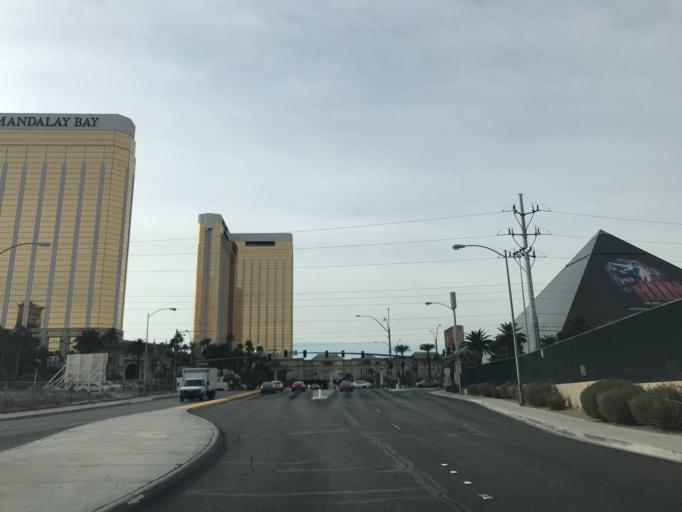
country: US
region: Nevada
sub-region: Clark County
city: Paradise
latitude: 36.0937
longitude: -115.1716
